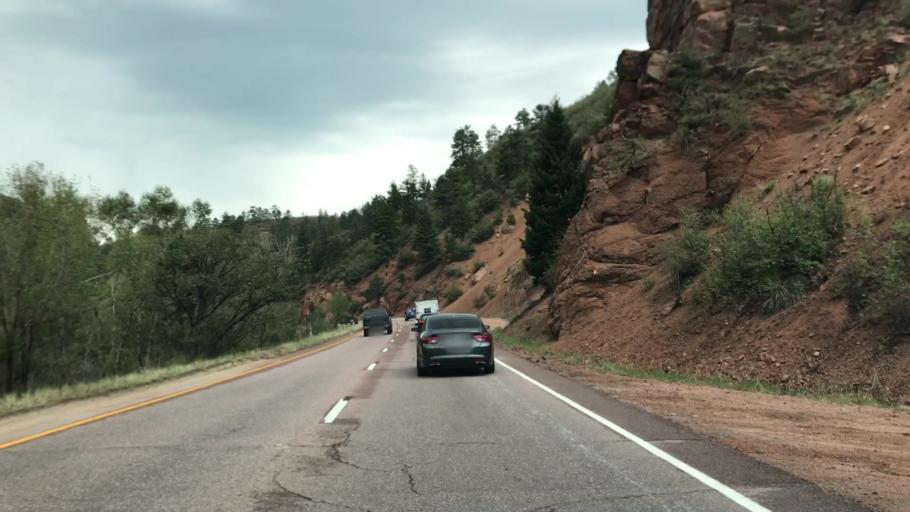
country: US
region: Colorado
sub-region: El Paso County
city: Manitou Springs
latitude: 38.8883
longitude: -104.9562
